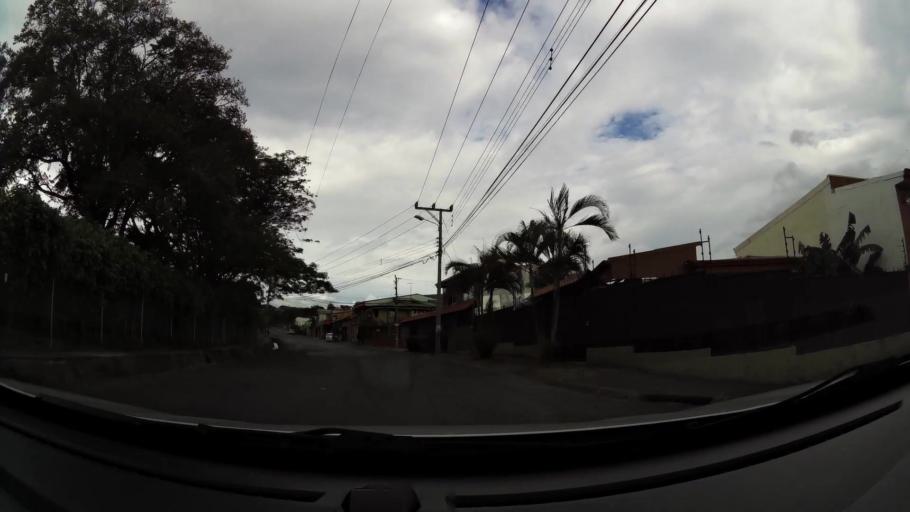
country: CR
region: Heredia
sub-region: Canton de Belen
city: San Antonio
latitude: 9.9665
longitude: -84.1906
